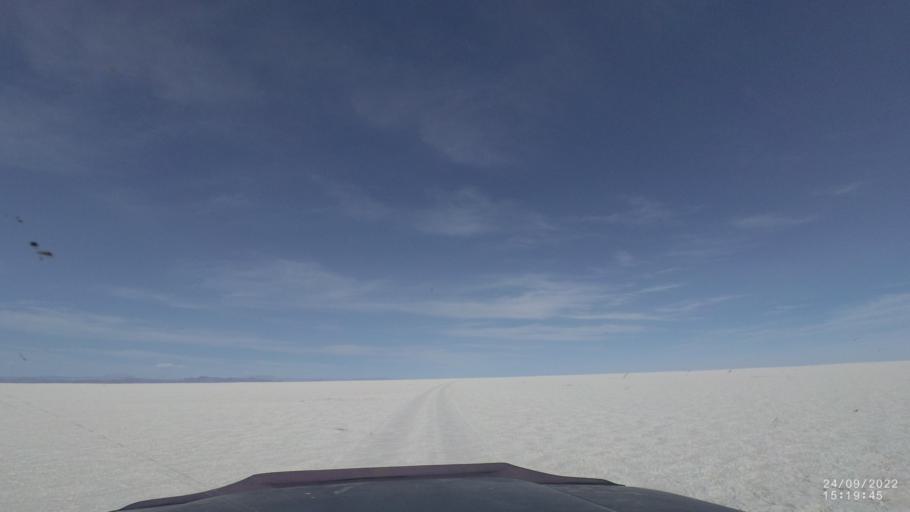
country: BO
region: Potosi
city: Colchani
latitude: -20.0066
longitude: -67.4060
